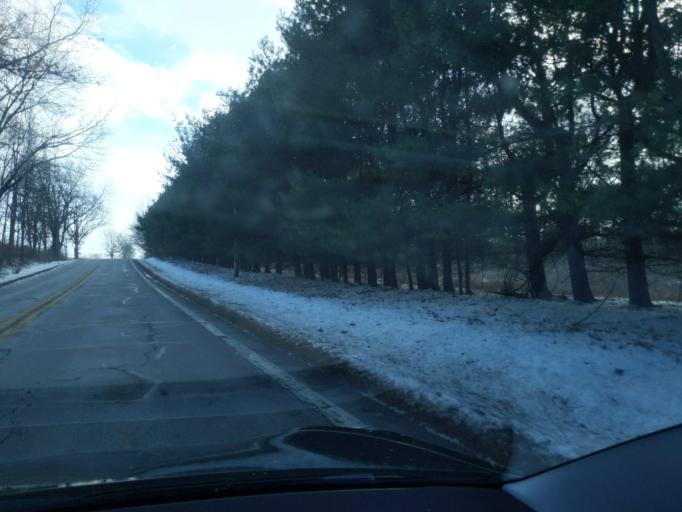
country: US
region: Michigan
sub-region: Ingham County
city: Stockbridge
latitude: 42.4864
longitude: -84.0921
